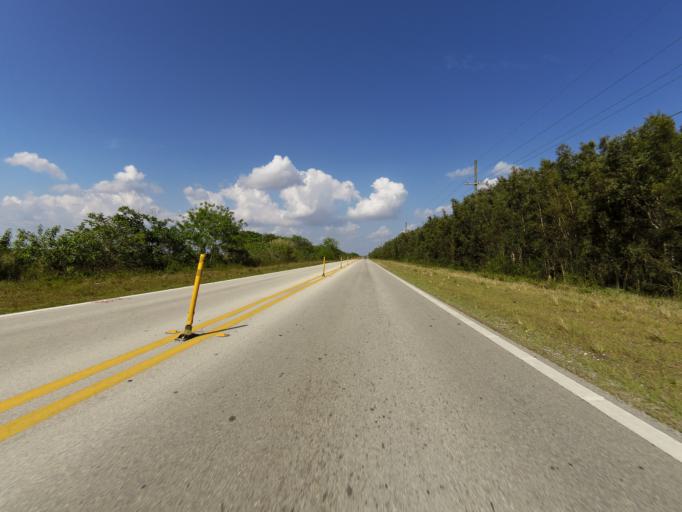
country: US
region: Florida
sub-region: Miami-Dade County
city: Palm Springs North
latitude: 25.9194
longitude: -80.4595
